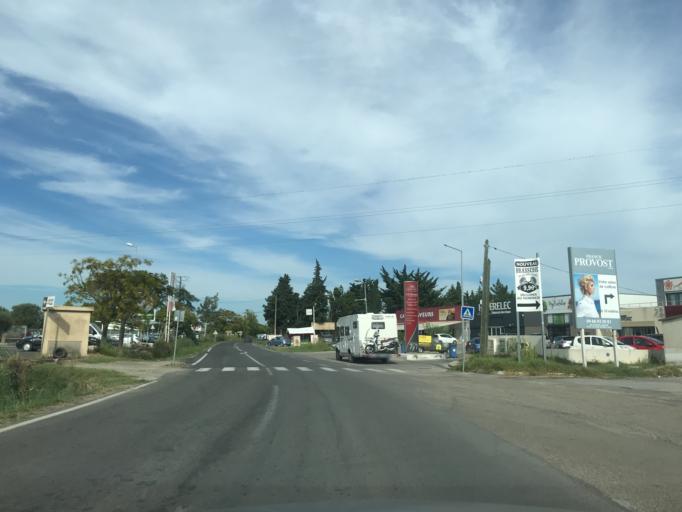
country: FR
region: Languedoc-Roussillon
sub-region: Departement du Gard
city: Aigues-Mortes
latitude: 43.5771
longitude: 4.1991
